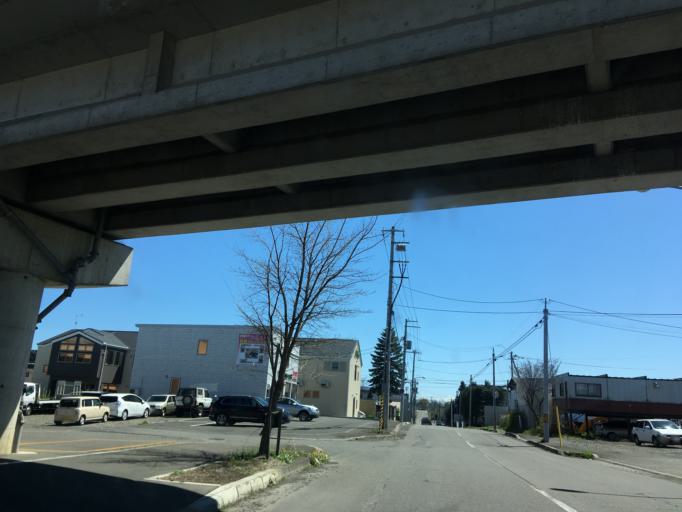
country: JP
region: Hokkaido
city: Obihiro
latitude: 42.9296
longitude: 143.1770
